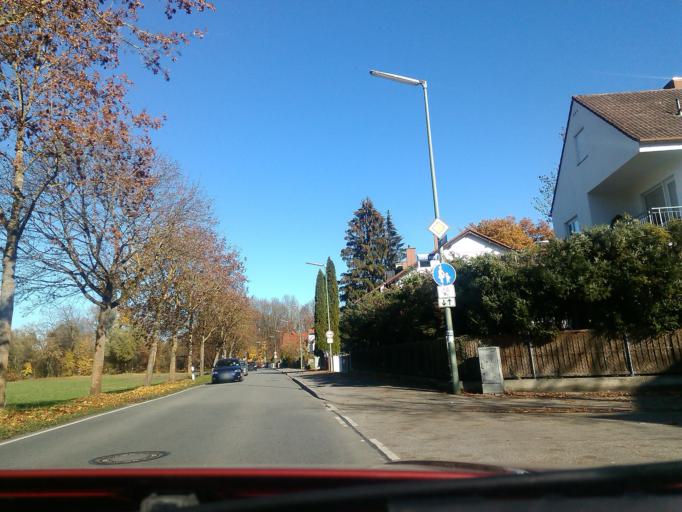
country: DE
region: Bavaria
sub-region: Upper Bavaria
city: Grobenzell
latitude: 48.1736
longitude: 11.4076
